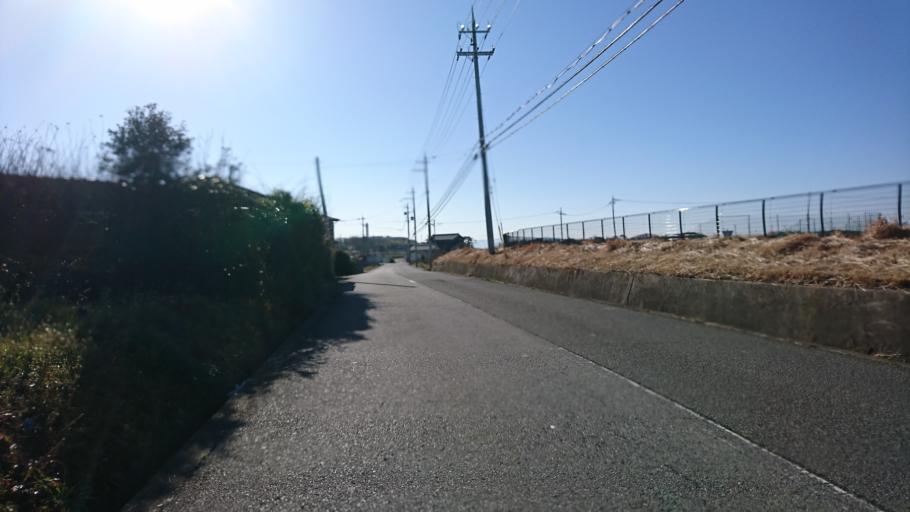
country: JP
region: Hyogo
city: Miki
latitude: 34.7188
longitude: 134.9609
